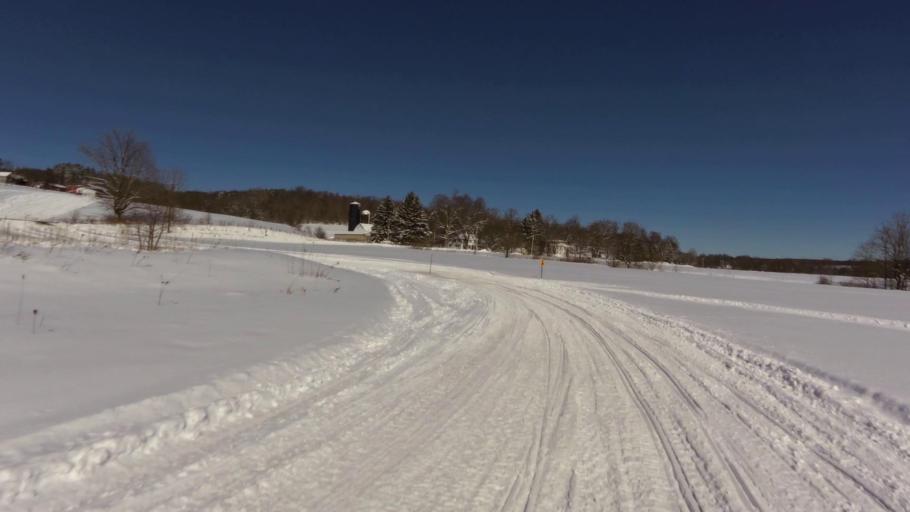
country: US
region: New York
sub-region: Chautauqua County
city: Mayville
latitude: 42.2506
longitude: -79.4398
